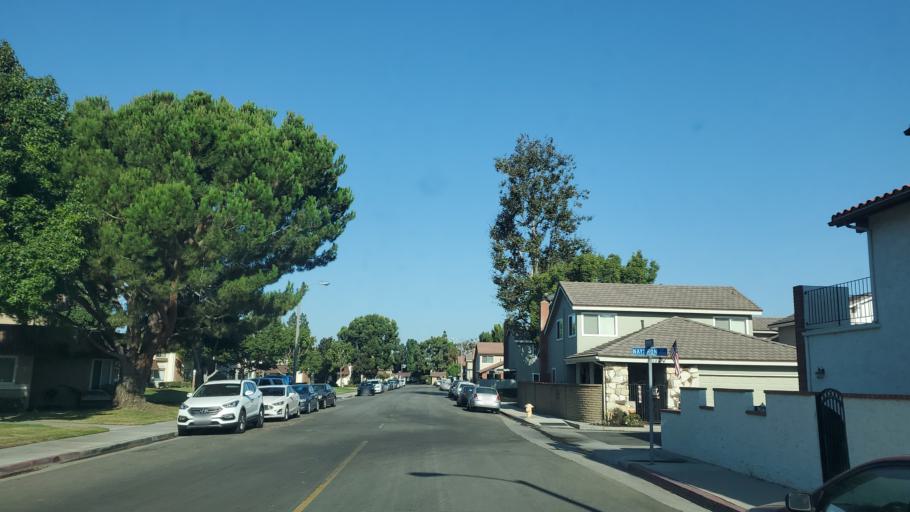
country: US
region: California
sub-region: Orange County
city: Stanton
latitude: 33.7966
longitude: -118.0164
